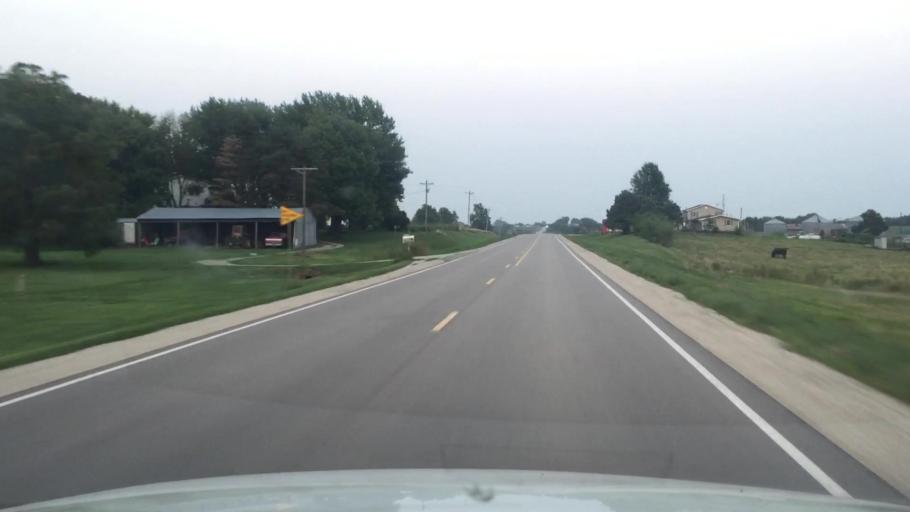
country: US
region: Iowa
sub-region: Warren County
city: Indianola
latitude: 41.1825
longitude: -93.4758
